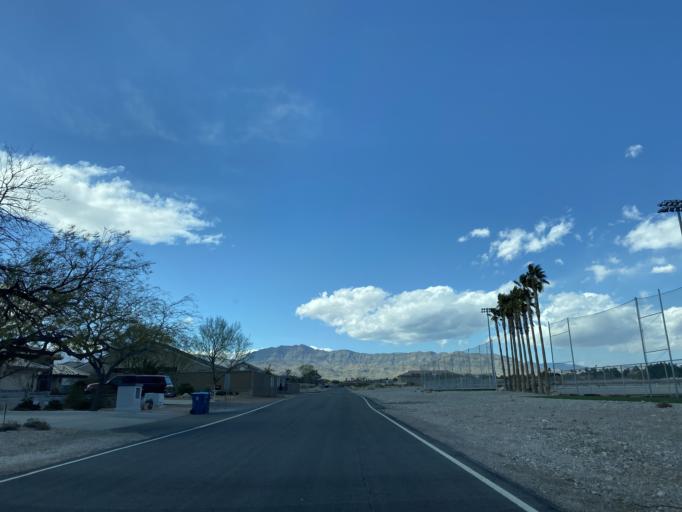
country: US
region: Nevada
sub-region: Clark County
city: Summerlin South
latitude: 36.2719
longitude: -115.2837
